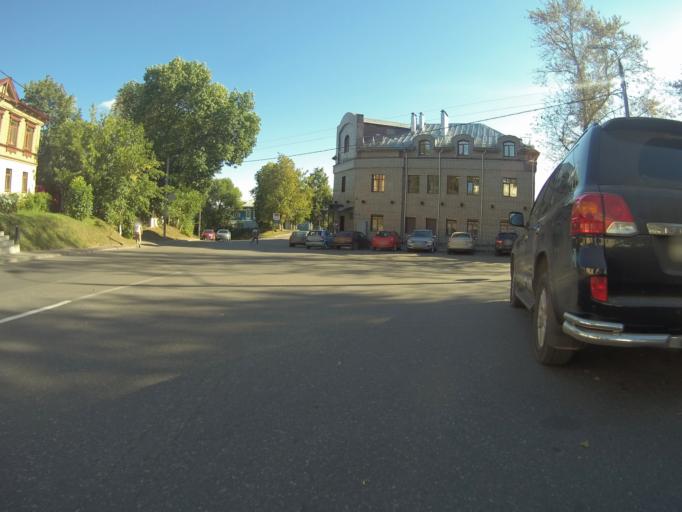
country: RU
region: Vladimir
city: Vladimir
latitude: 56.1245
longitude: 40.3977
